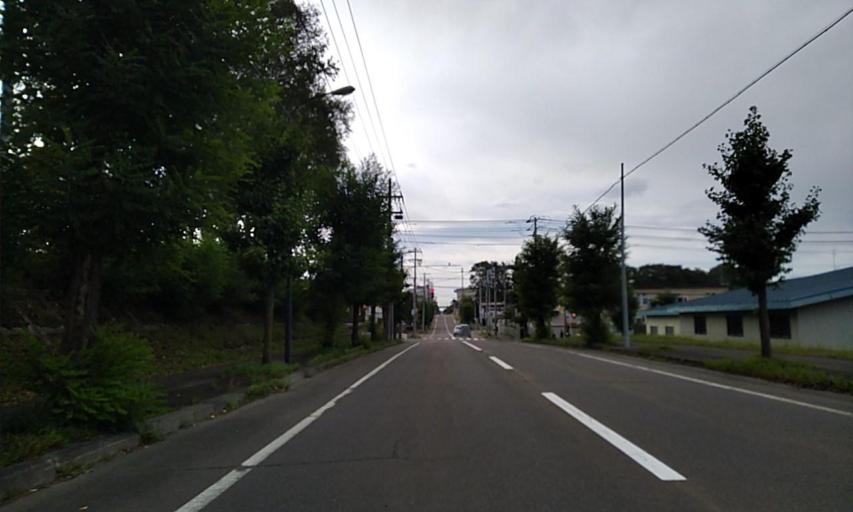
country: JP
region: Hokkaido
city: Obihiro
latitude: 42.9160
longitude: 143.0423
